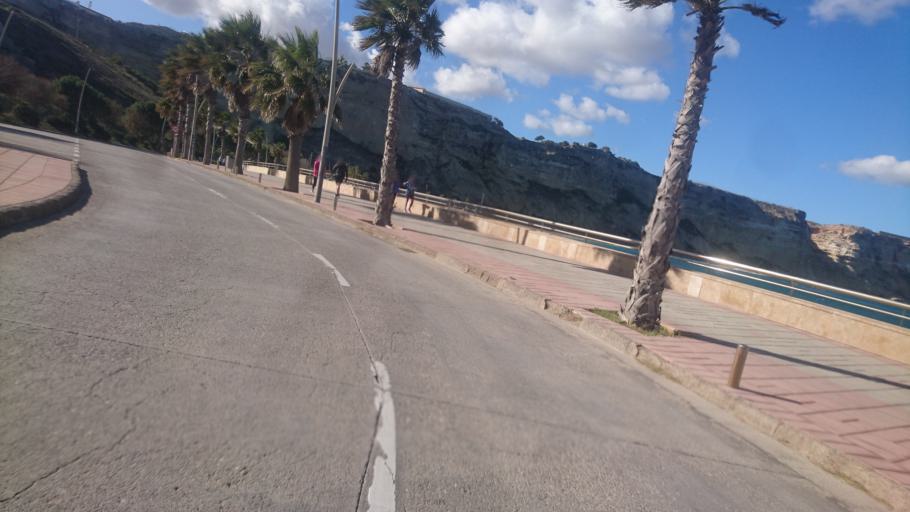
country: ES
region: Melilla
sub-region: Melilla
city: Melilla
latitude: 35.3032
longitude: -2.9389
